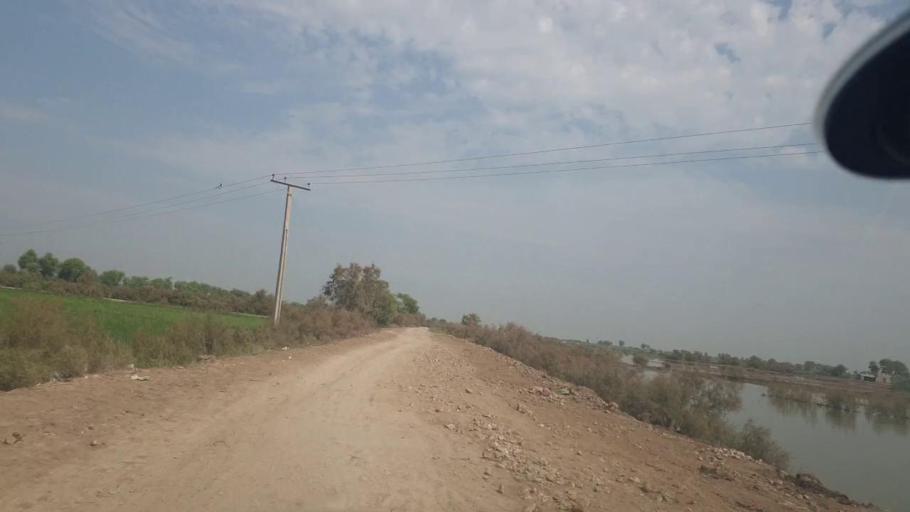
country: PK
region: Balochistan
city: Mehrabpur
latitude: 28.1061
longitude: 68.0914
